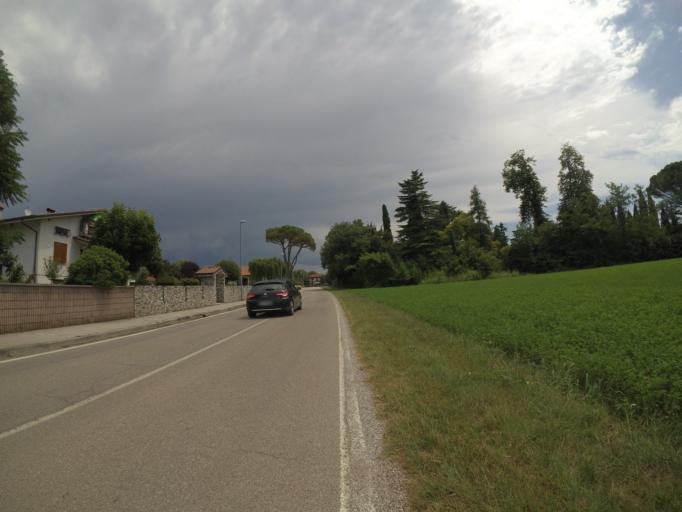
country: IT
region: Friuli Venezia Giulia
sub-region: Provincia di Udine
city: Talmassons
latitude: 45.9224
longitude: 13.1378
